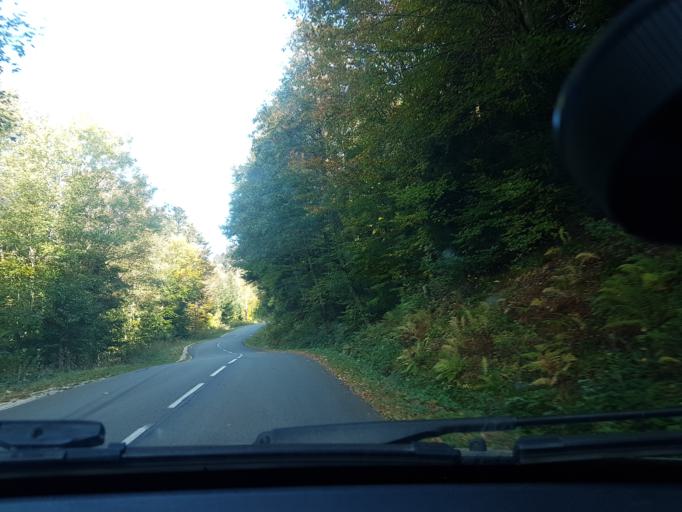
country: FR
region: Franche-Comte
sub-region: Departement de la Haute-Saone
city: Plancher-les-Mines
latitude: 47.7752
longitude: 6.7630
